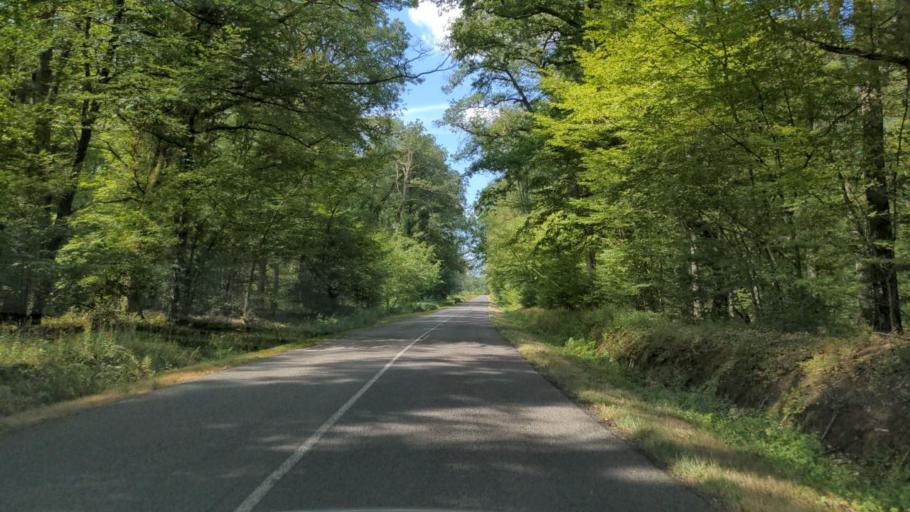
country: FR
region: Auvergne
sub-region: Departement de l'Allier
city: Buxieres-les-Mines
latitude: 46.5012
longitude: 2.9665
